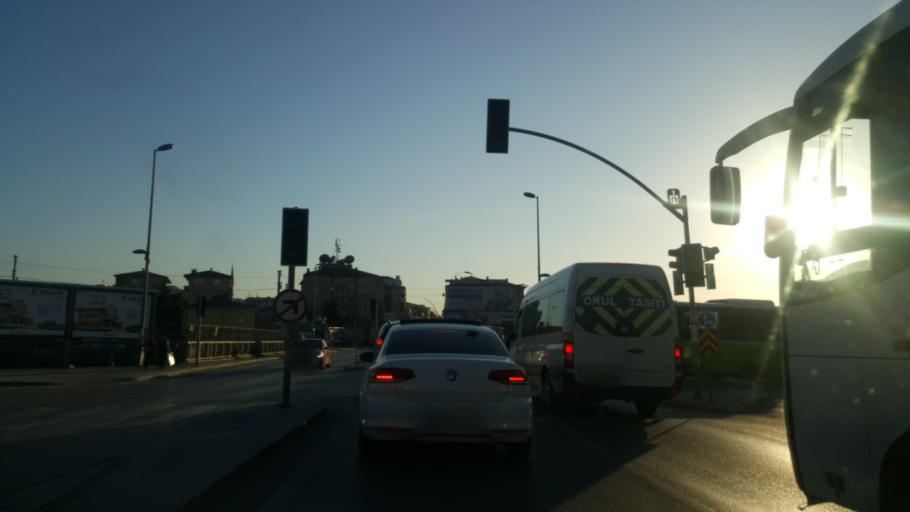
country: TR
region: Kocaeli
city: Darica
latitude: 40.7835
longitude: 29.4136
